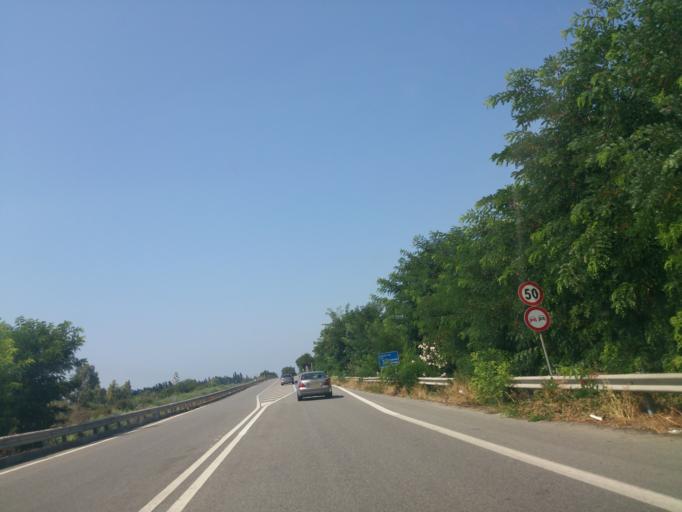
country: IT
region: Calabria
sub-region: Provincia di Reggio Calabria
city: Caulonia Marina
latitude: 38.3581
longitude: 16.4872
